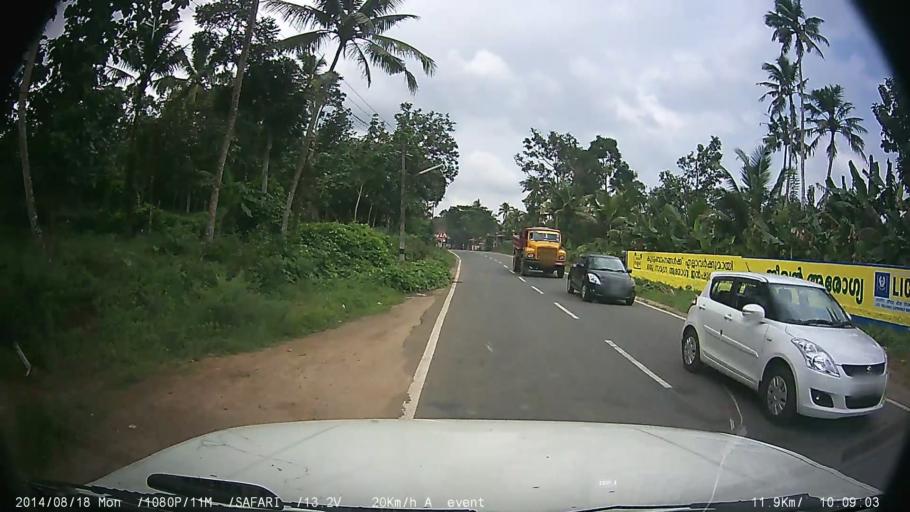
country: IN
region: Kerala
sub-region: Kottayam
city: Palackattumala
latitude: 9.7204
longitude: 76.5604
